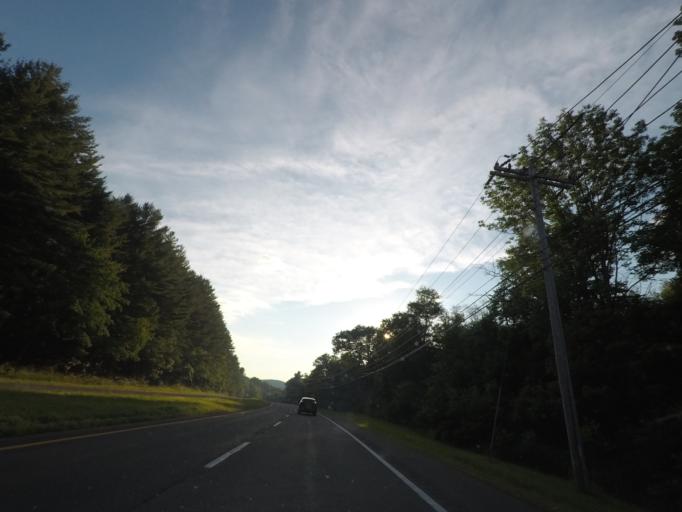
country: US
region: Massachusetts
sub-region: Hampden County
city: Brimfield
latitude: 42.1190
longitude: -72.2408
